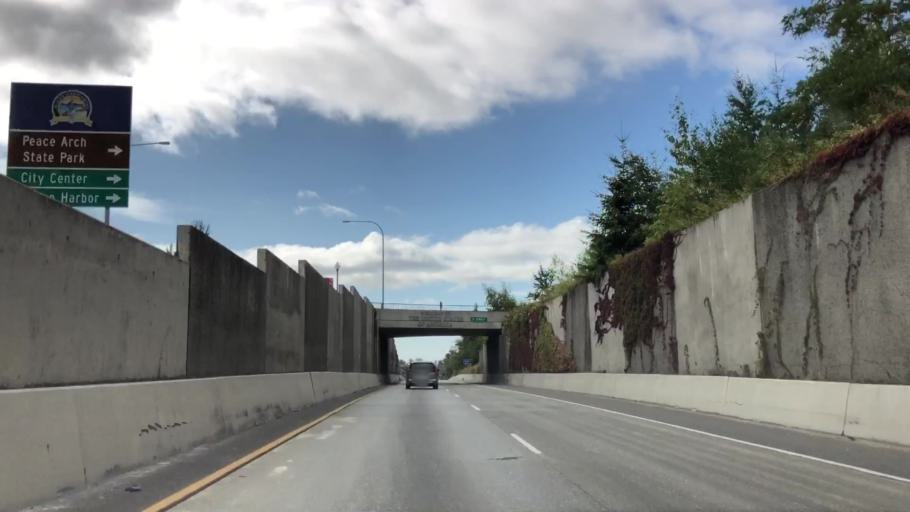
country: US
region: Washington
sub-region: Whatcom County
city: Blaine
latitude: 48.9989
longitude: -122.7352
